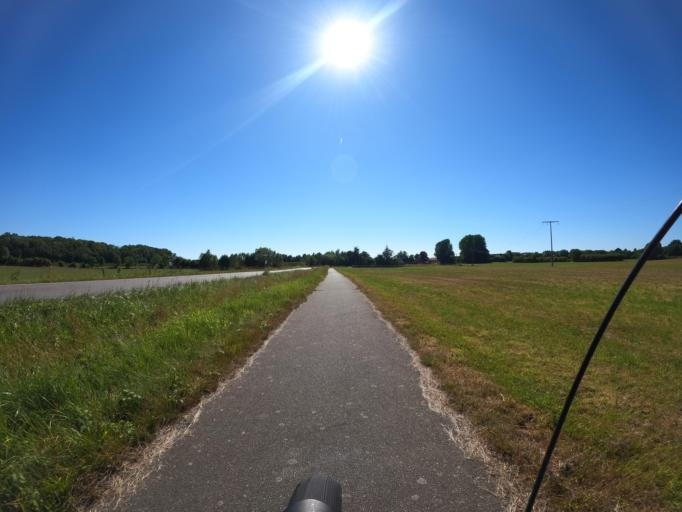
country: DE
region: Schleswig-Holstein
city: Steinberg
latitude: 54.7774
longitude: 9.7808
